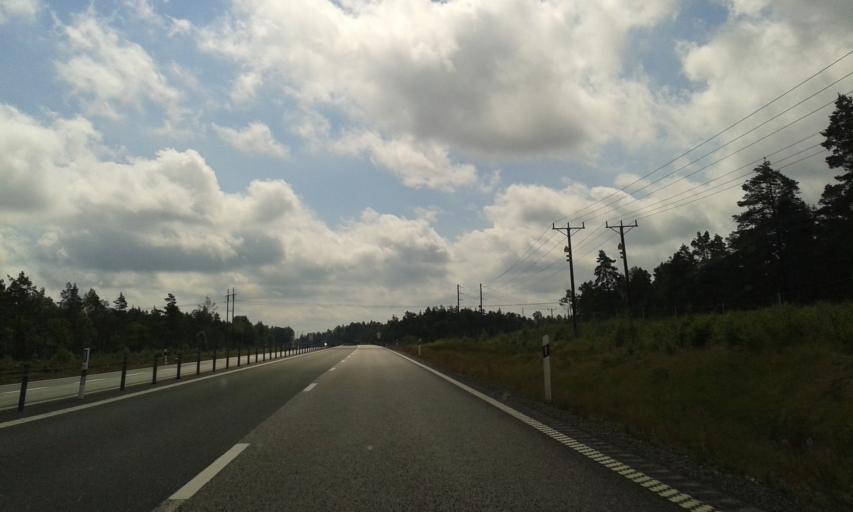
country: SE
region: Joenkoeping
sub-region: Gislaveds Kommun
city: Gislaved
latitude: 57.2984
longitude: 13.5856
